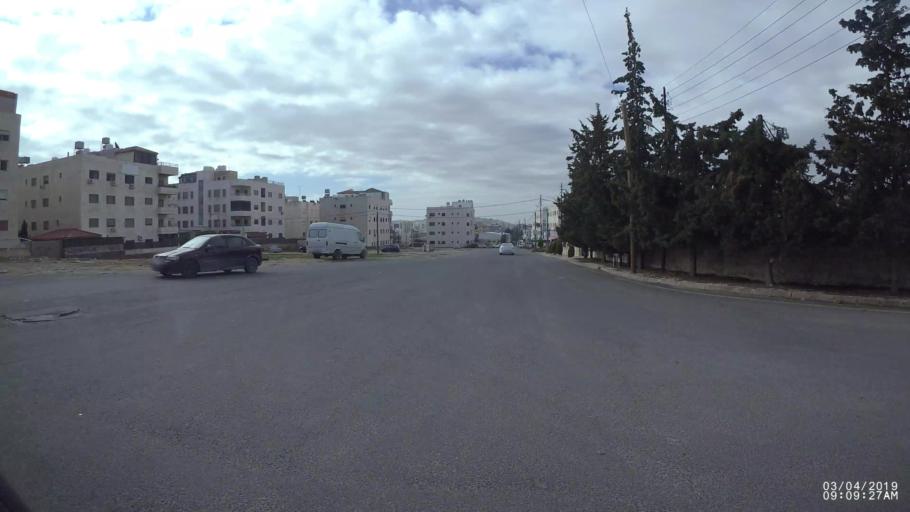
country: JO
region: Amman
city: Wadi as Sir
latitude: 31.9476
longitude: 35.8481
